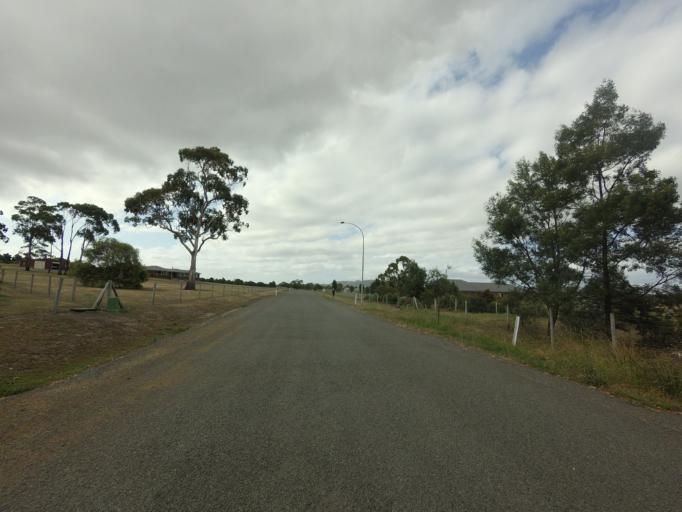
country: AU
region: Tasmania
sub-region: Clarence
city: Cambridge
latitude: -42.8393
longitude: 147.4693
